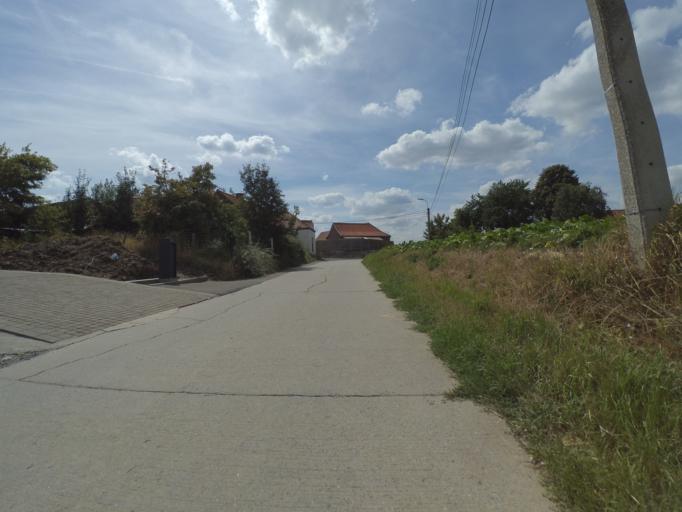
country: BE
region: Flanders
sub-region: Provincie Oost-Vlaanderen
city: Ronse
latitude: 50.7955
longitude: 3.6445
